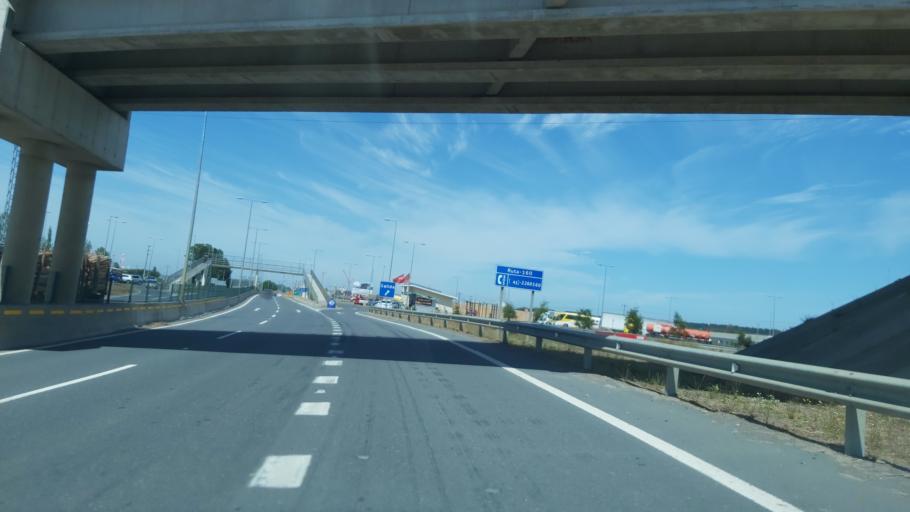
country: CL
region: Biobio
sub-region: Provincia de Concepcion
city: Lota
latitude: -37.1859
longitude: -73.1965
